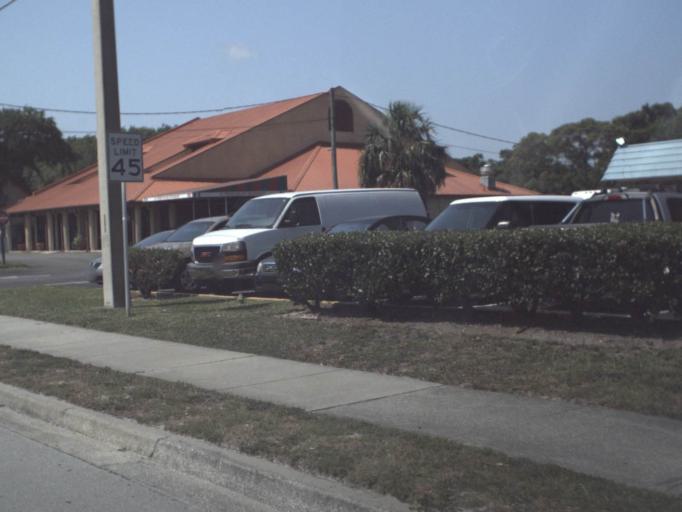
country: US
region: Florida
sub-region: Saint Johns County
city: Butler Beach
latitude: 29.8214
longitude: -81.2705
